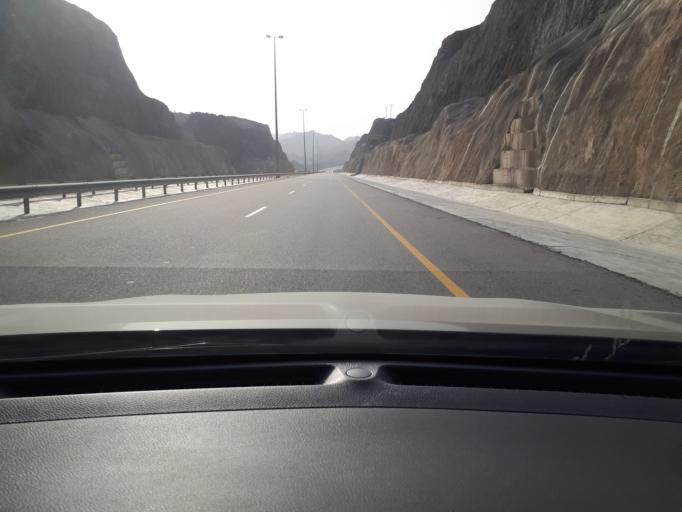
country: OM
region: Muhafazat Masqat
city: Muscat
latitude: 23.2080
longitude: 58.8077
